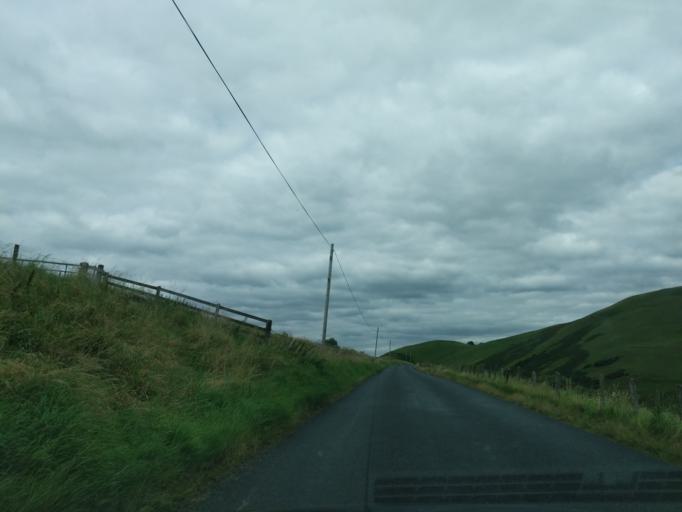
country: GB
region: Scotland
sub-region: The Scottish Borders
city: West Linton
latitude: 55.6900
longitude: -3.3340
